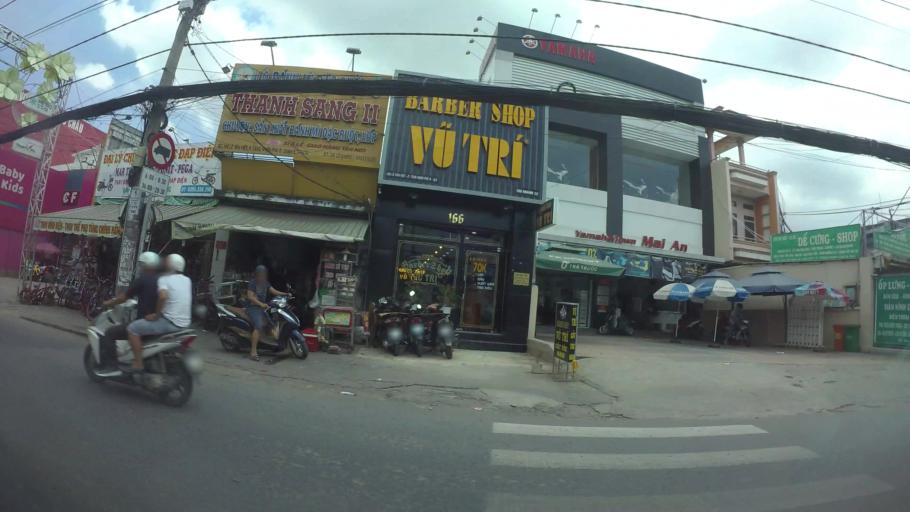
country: VN
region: Ho Chi Minh City
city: Thu Duc
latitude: 10.8435
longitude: 106.7811
